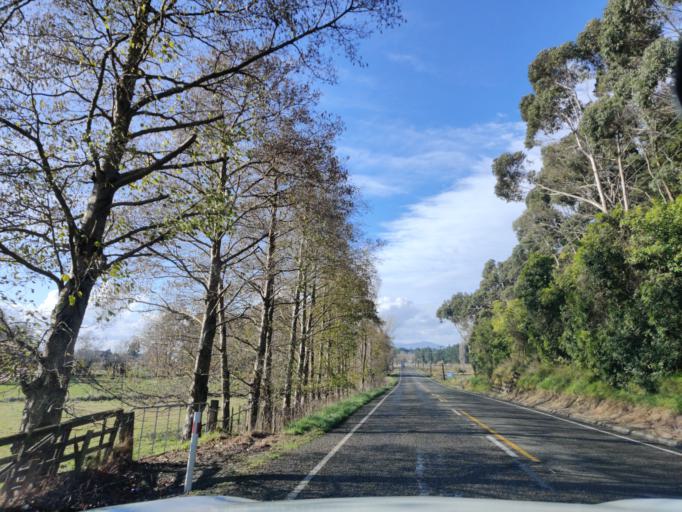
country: NZ
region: Manawatu-Wanganui
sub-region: Palmerston North City
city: Palmerston North
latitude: -40.3719
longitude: 175.6533
